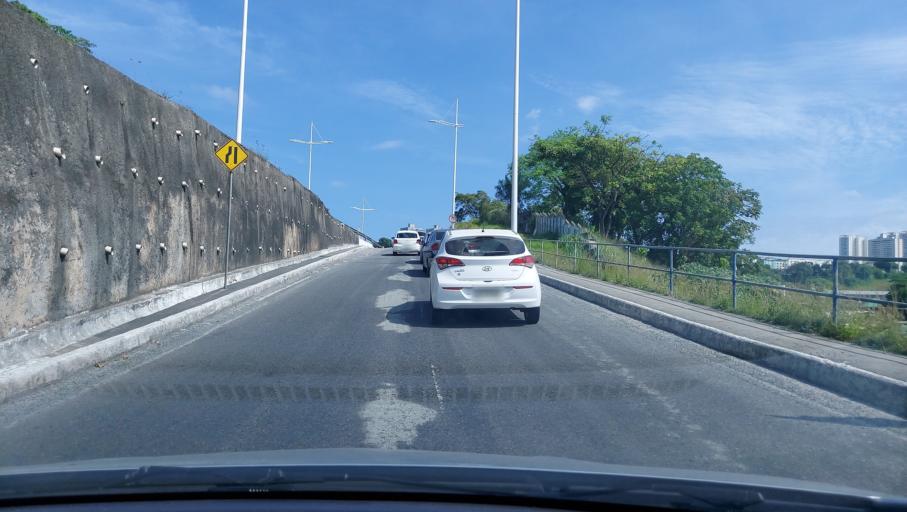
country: BR
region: Bahia
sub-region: Salvador
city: Salvador
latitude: -12.9527
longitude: -38.4743
